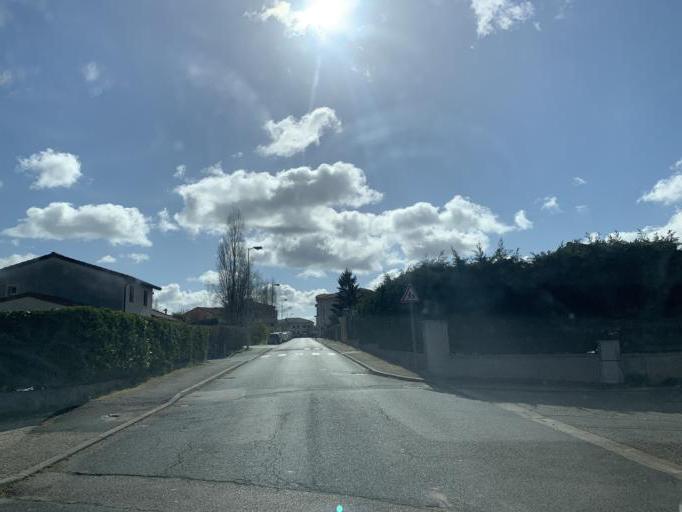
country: FR
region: Rhone-Alpes
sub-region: Departement de l'Ain
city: Saint-Andre-de-Corcy
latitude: 45.9500
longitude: 4.9838
